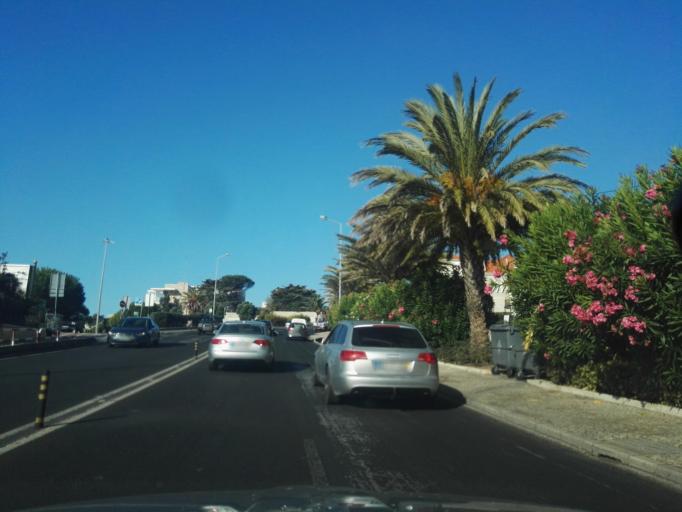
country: PT
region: Lisbon
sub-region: Cascais
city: Estoril
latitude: 38.7028
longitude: -9.3926
